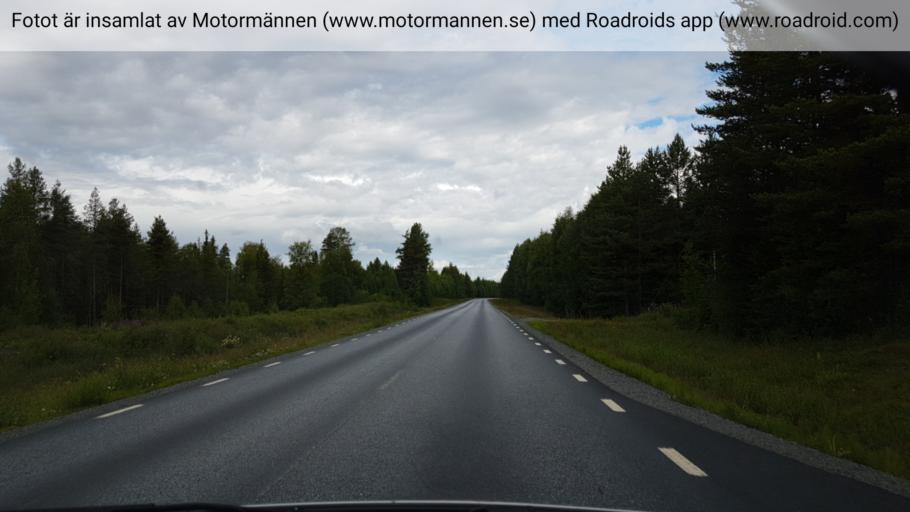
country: SE
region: Vaesterbotten
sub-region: Vilhelmina Kommun
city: Vilhelmina
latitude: 64.4778
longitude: 16.7882
